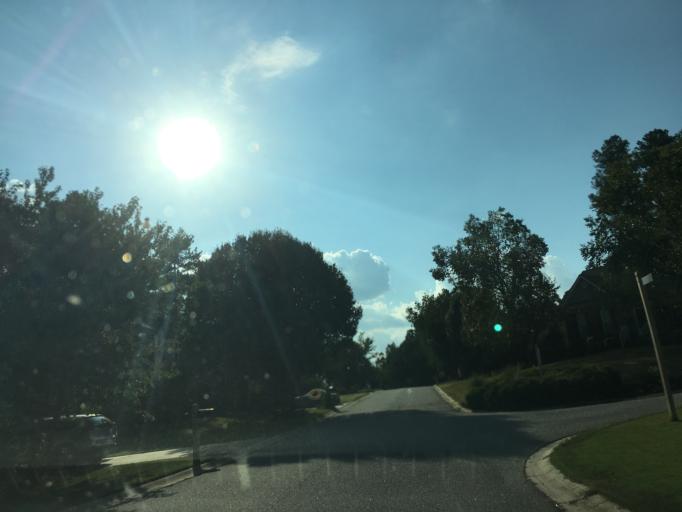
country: US
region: South Carolina
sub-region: Richland County
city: Lake Murray of Richland
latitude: 34.1450
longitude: -81.2227
